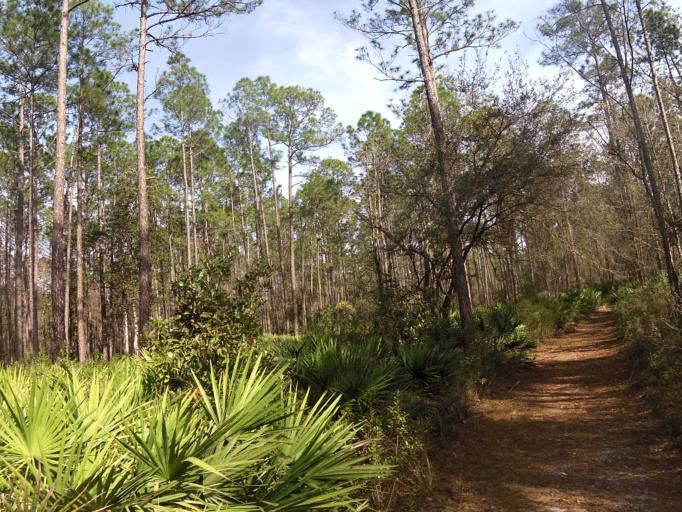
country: US
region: Florida
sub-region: Clay County
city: Middleburg
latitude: 30.1151
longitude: -81.9022
